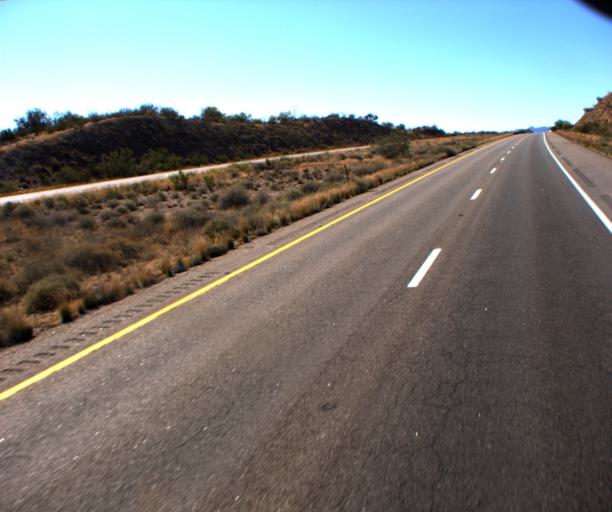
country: US
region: Arizona
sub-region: Yavapai County
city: Bagdad
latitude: 34.6173
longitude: -113.5290
